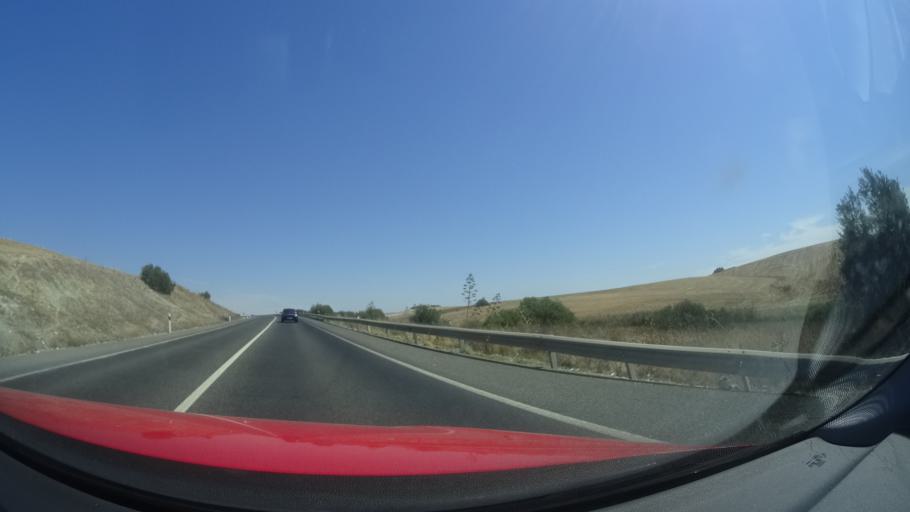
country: ES
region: Andalusia
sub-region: Provincia de Sevilla
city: Las Cabezas de San Juan
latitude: 36.9272
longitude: -5.9290
